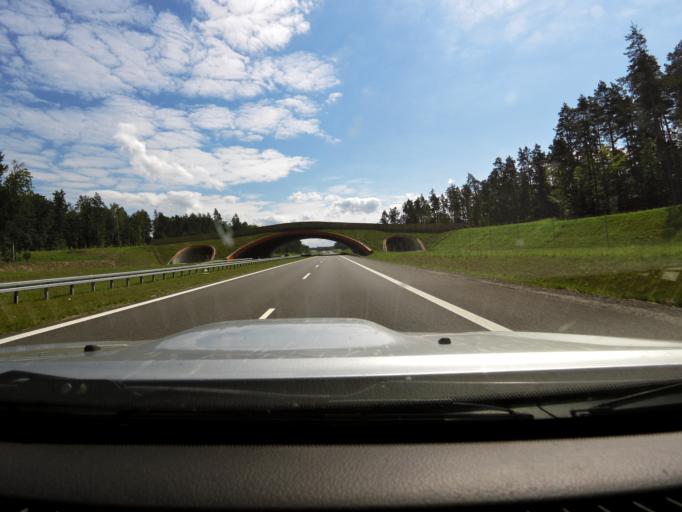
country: PL
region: Warmian-Masurian Voivodeship
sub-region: Powiat ostrodzki
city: Milomlyn
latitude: 53.7525
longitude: 19.8736
